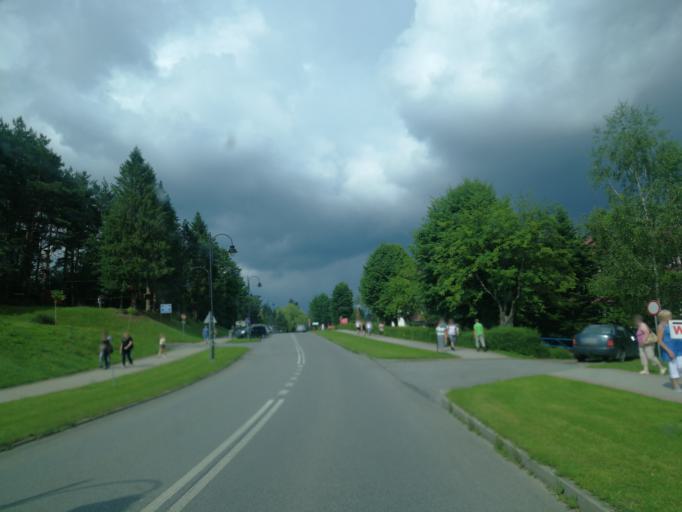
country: PL
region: Subcarpathian Voivodeship
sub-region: Powiat leski
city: Polanczyk
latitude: 49.3725
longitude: 22.4328
